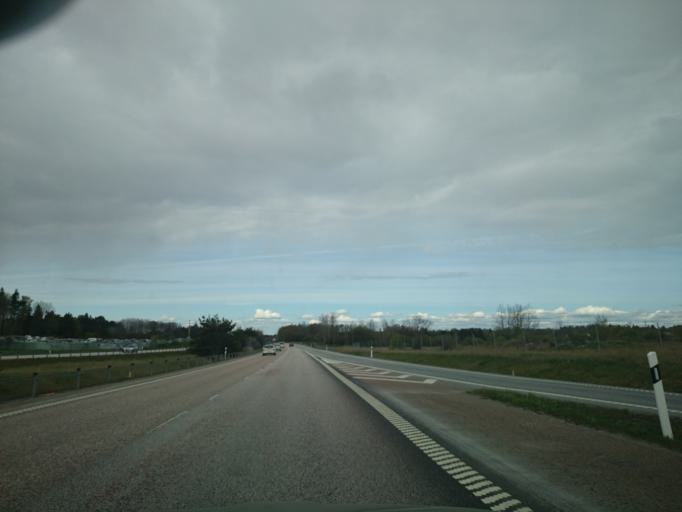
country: SE
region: Stockholm
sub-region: Sigtuna Kommun
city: Marsta
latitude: 59.6331
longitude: 17.8993
